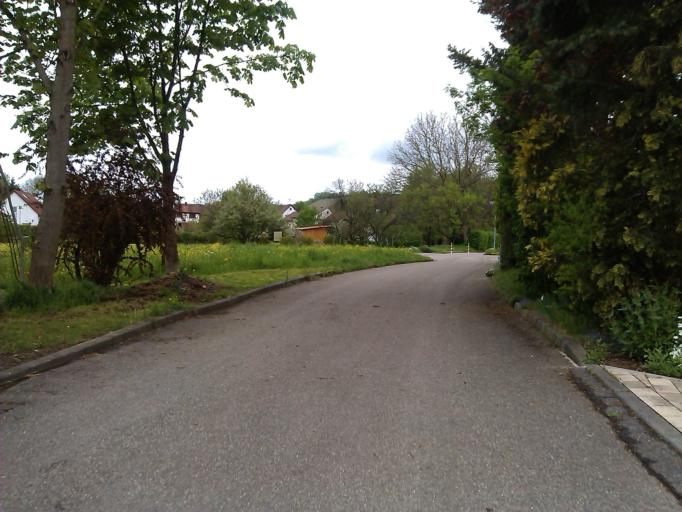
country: DE
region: Baden-Wuerttemberg
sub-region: Regierungsbezirk Stuttgart
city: Zaberfeld
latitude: 49.0586
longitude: 8.9298
